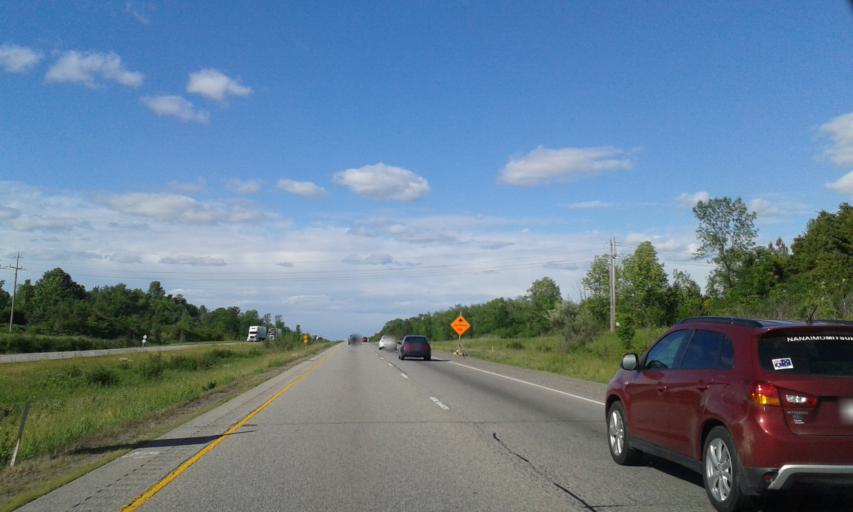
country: CA
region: Ontario
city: Prescott
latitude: 44.6711
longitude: -75.6042
